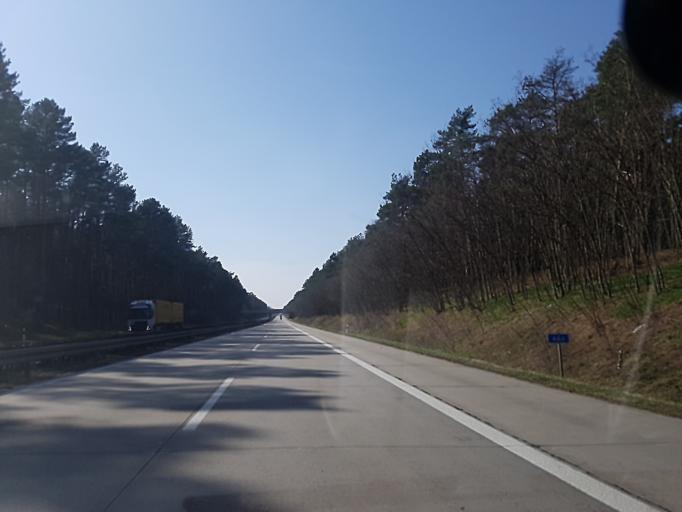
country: DE
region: Brandenburg
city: Heinersbruck
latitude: 51.7100
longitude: 14.5156
